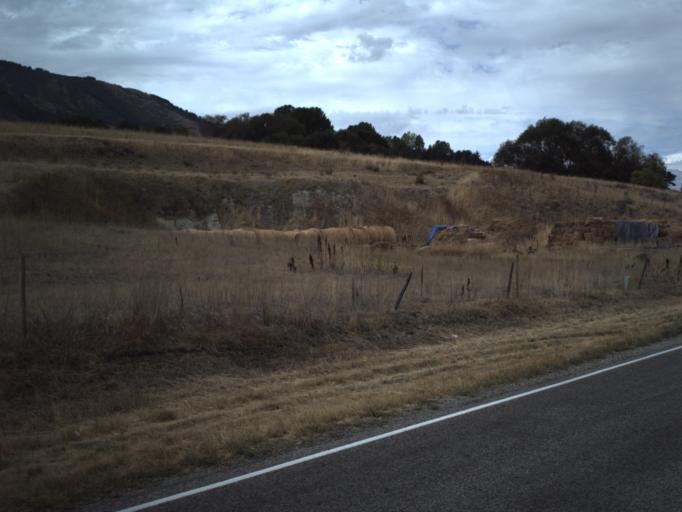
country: US
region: Utah
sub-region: Cache County
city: Mendon
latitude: 41.6950
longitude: -111.9726
